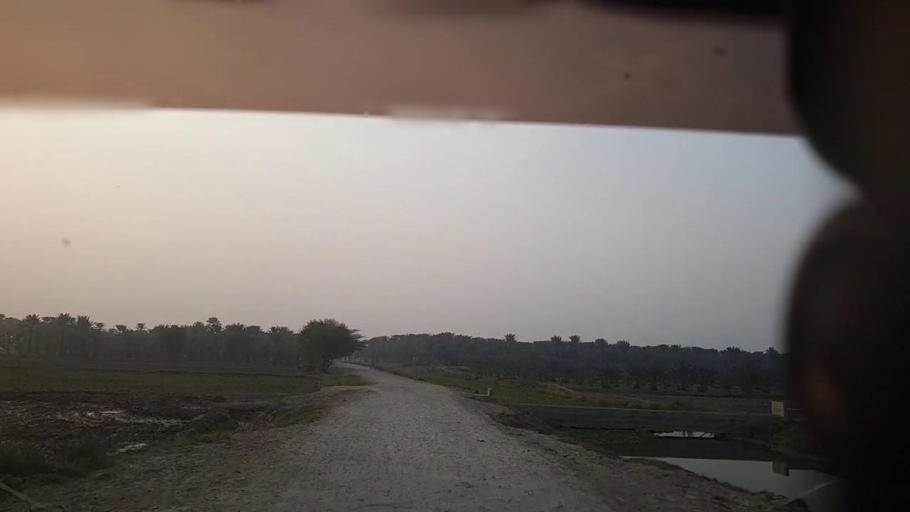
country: PK
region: Sindh
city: Pir jo Goth
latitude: 27.5219
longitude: 68.6442
